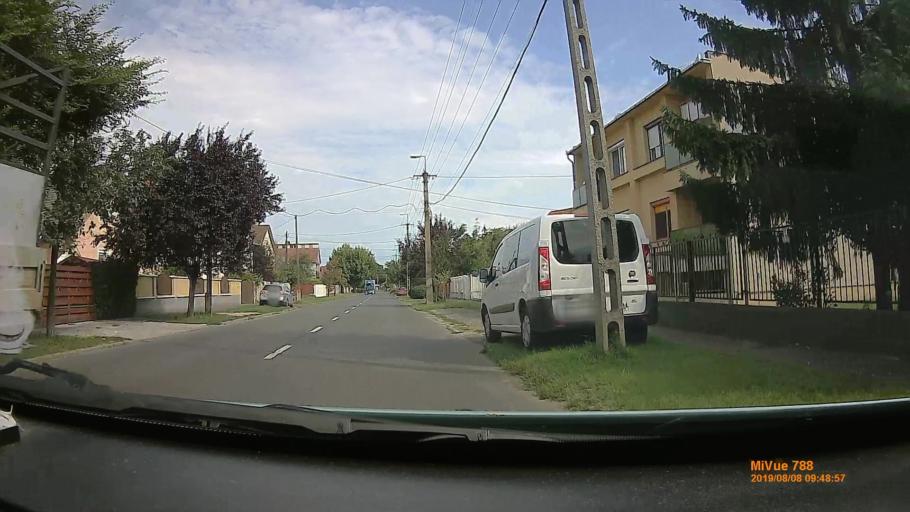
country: HU
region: Hajdu-Bihar
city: Debrecen
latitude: 47.5439
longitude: 21.6535
